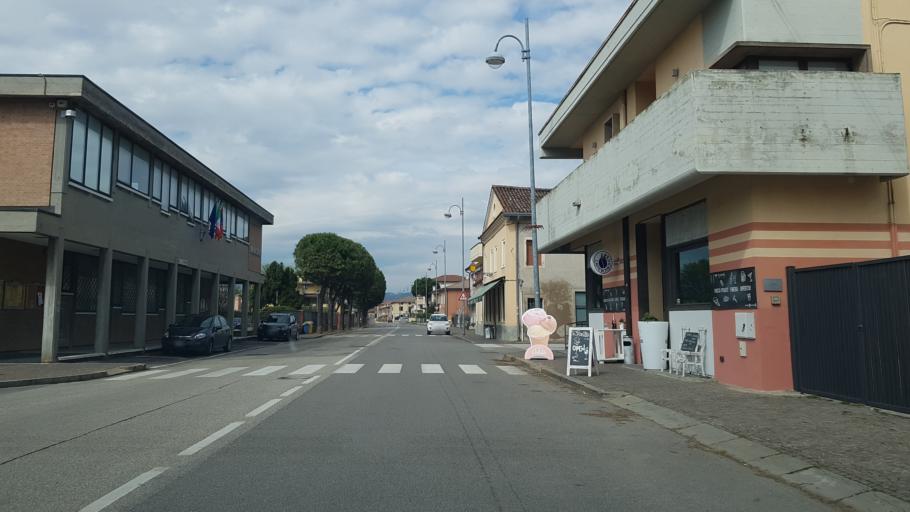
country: IT
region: Veneto
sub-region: Provincia di Verona
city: Belfiore
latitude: 45.3799
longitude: 11.2092
